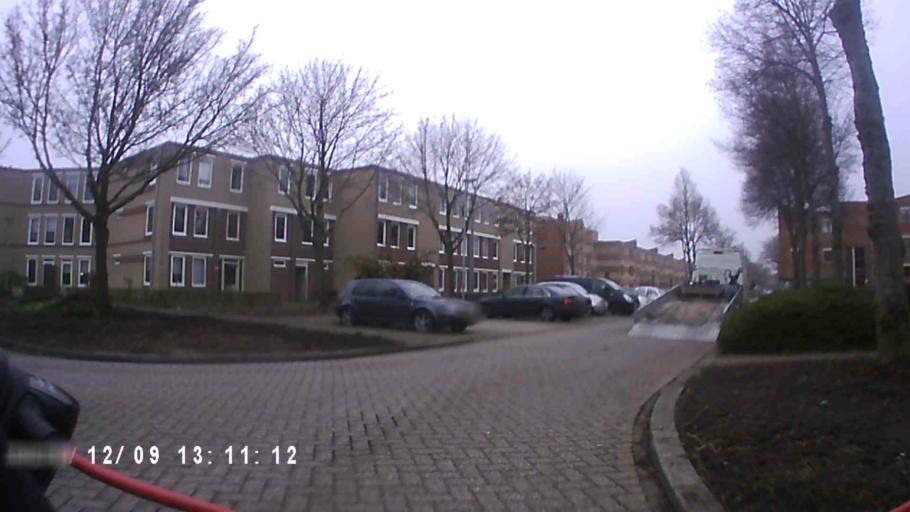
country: NL
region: Groningen
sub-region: Gemeente Groningen
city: Oosterpark
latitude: 53.2469
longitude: 6.6050
